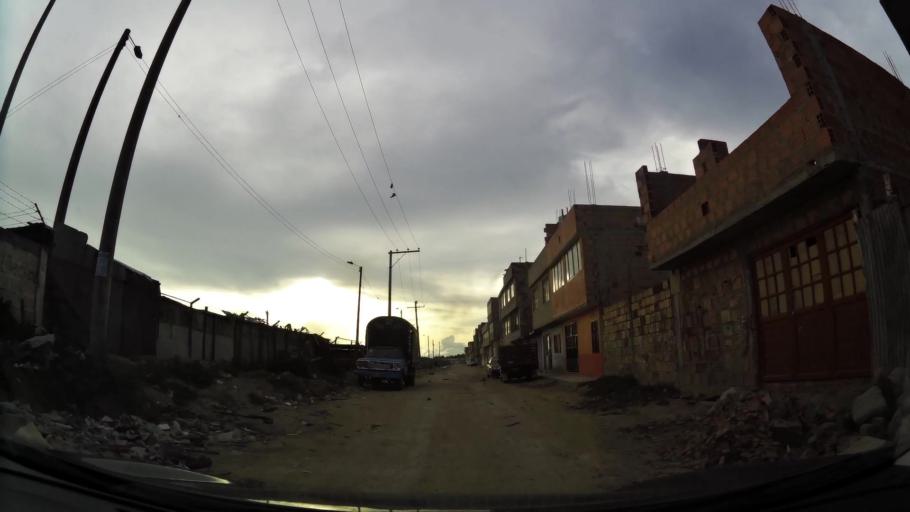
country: CO
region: Cundinamarca
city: Funza
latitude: 4.6906
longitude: -74.1722
